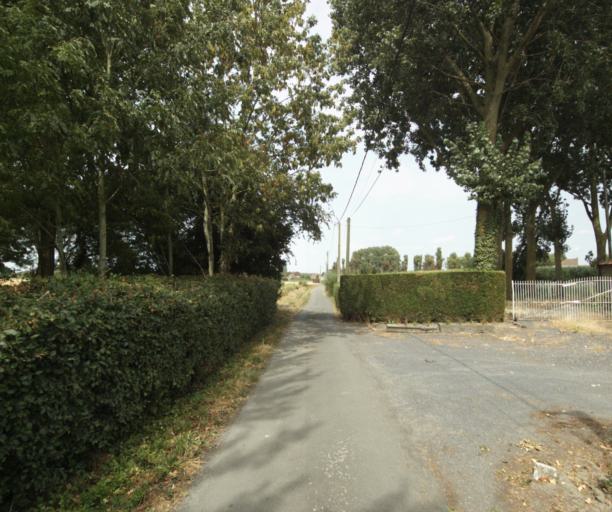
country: BE
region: Wallonia
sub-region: Province du Hainaut
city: Estaimpuis
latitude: 50.7006
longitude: 3.2500
